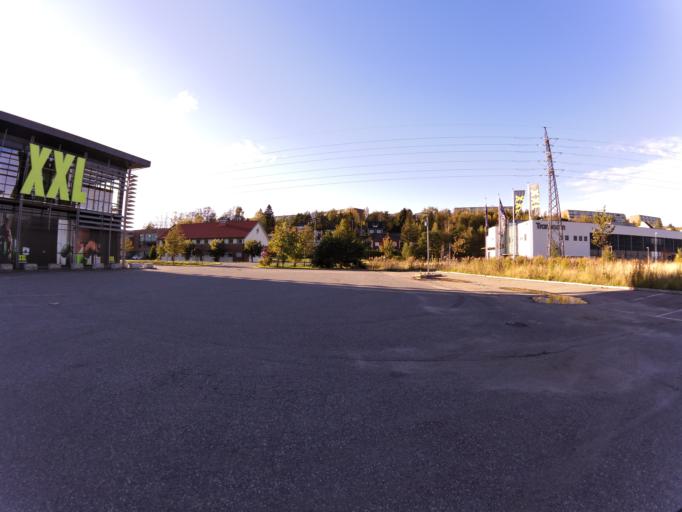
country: NO
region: Ostfold
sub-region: Fredrikstad
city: Fredrikstad
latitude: 59.2564
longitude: 11.0031
